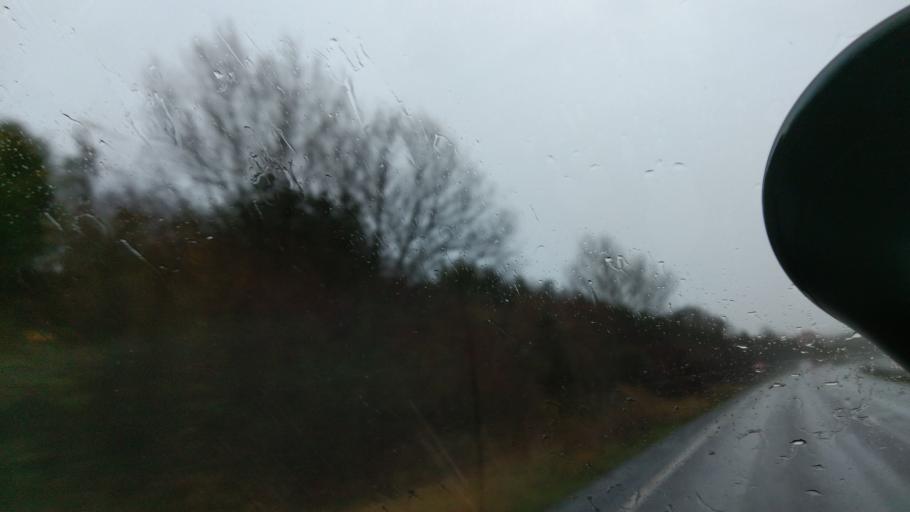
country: GB
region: England
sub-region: East Sussex
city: Portslade
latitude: 50.8478
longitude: -0.2457
